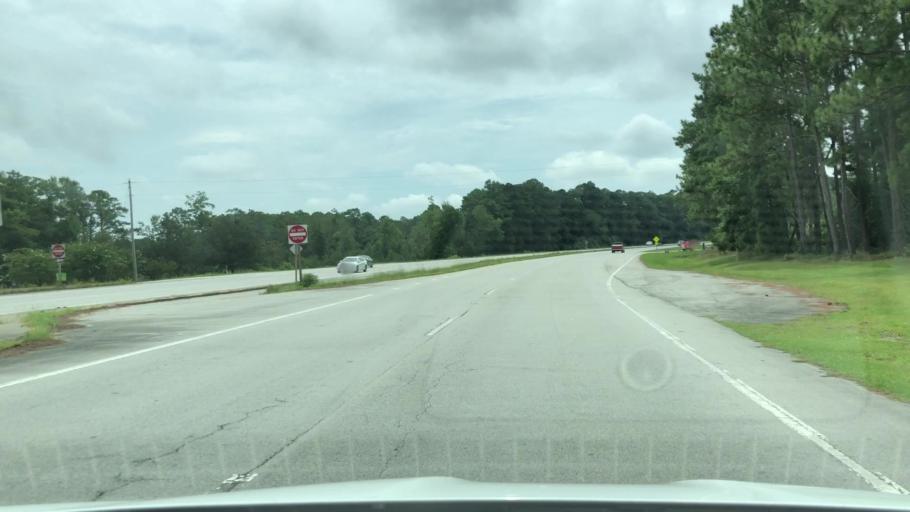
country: US
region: North Carolina
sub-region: Carteret County
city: Newport
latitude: 34.8256
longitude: -76.8762
